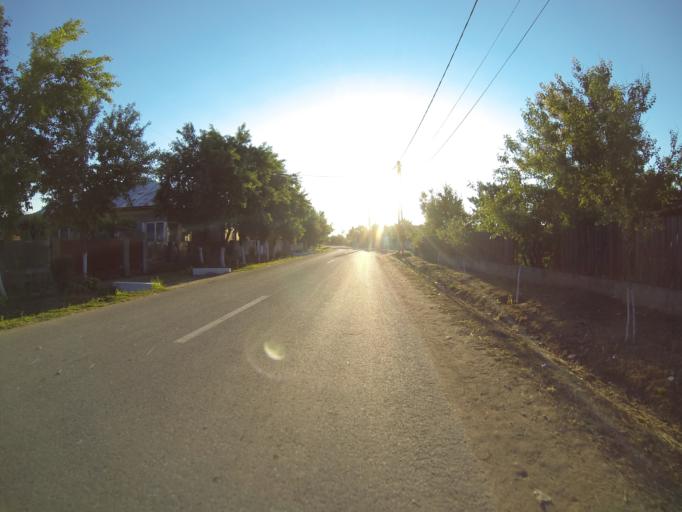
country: RO
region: Dolj
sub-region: Comuna Caloparu
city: Calopar
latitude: 44.1640
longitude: 23.7620
